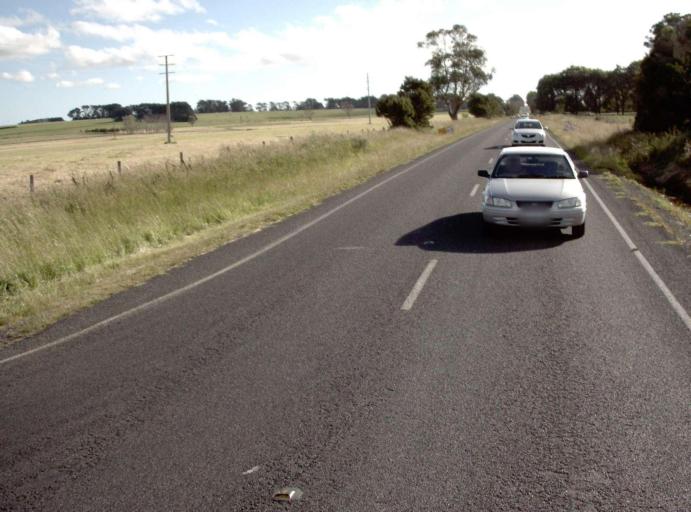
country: AU
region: Victoria
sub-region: Bass Coast
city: North Wonthaggi
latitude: -38.5035
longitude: 145.9147
